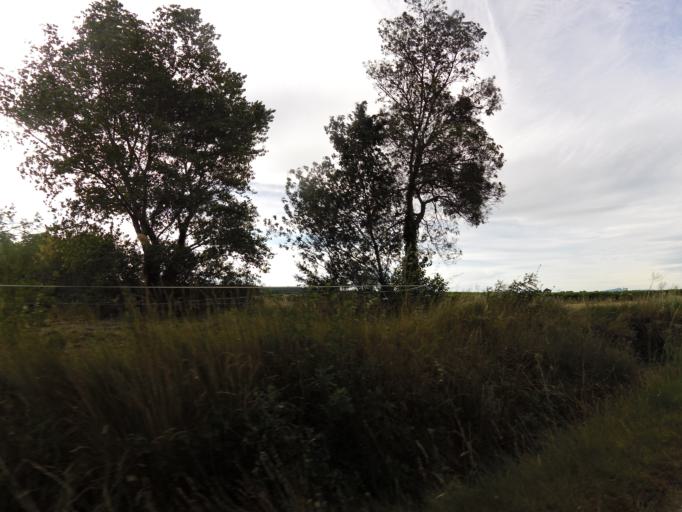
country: FR
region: Languedoc-Roussillon
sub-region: Departement du Gard
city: Saint-Mamert-du-Gard
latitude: 43.8940
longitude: 4.1984
